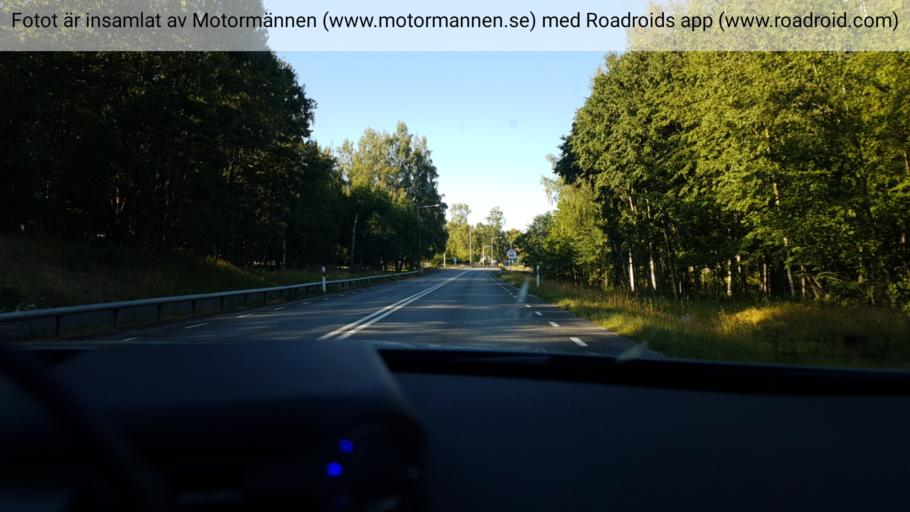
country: SE
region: Joenkoeping
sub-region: Habo Kommun
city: Habo
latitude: 58.0143
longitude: 14.1428
